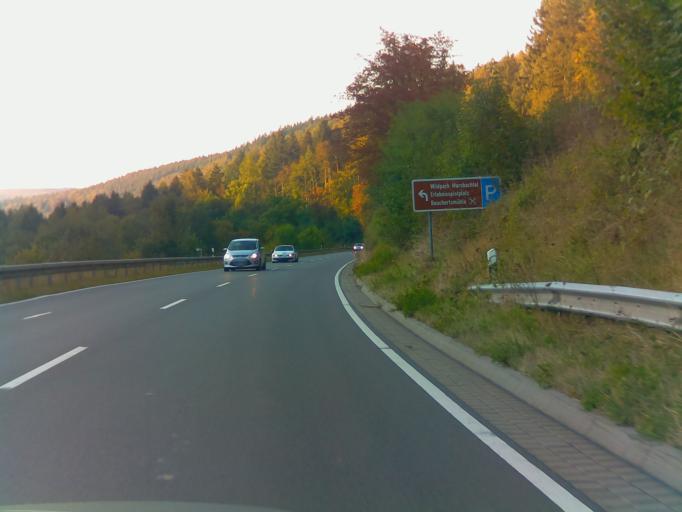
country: DE
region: Baden-Wuerttemberg
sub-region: Karlsruhe Region
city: Walldurn
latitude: 49.6018
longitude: 9.3428
